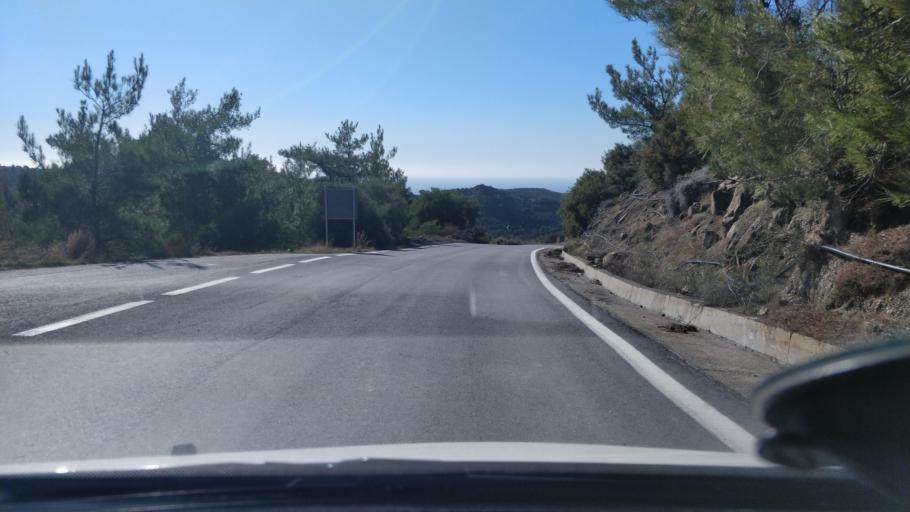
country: GR
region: Crete
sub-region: Nomos Irakleiou
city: Kastelli
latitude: 35.0232
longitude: 25.4483
